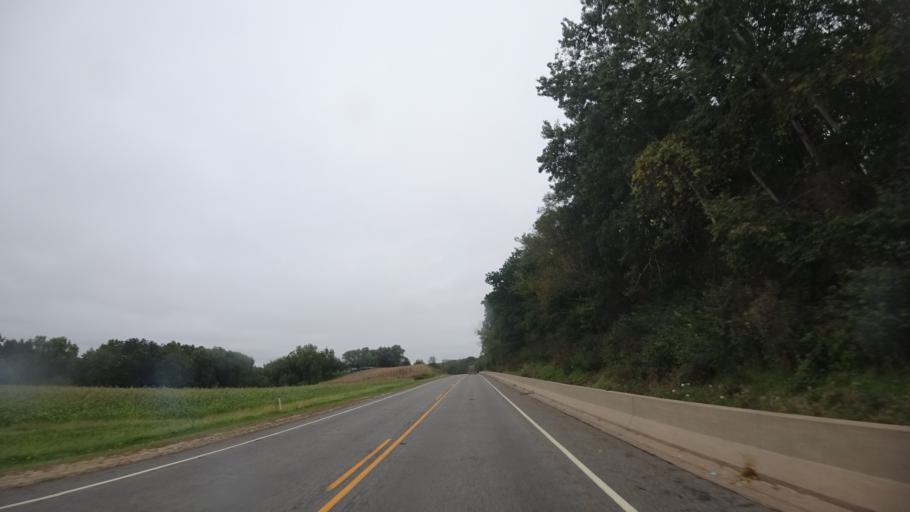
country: US
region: Wisconsin
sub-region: Crawford County
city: Prairie du Chien
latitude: 43.0521
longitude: -90.9770
